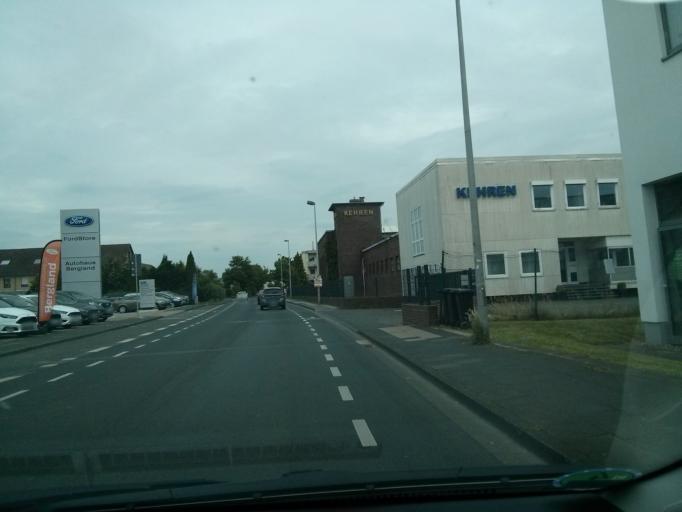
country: DE
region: North Rhine-Westphalia
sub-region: Regierungsbezirk Koln
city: Hennef
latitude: 50.7708
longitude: 7.2866
